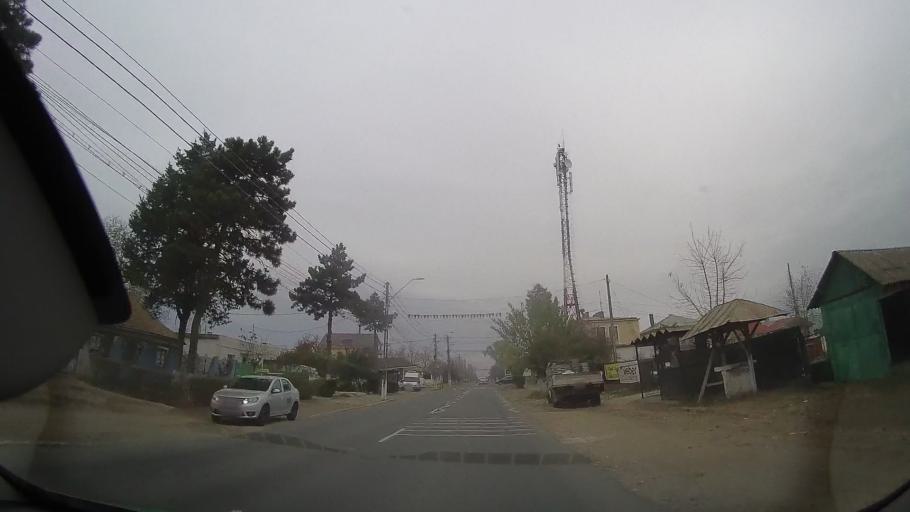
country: RO
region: Ialomita
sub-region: Oras Amara
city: Amara
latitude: 44.6139
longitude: 27.3143
